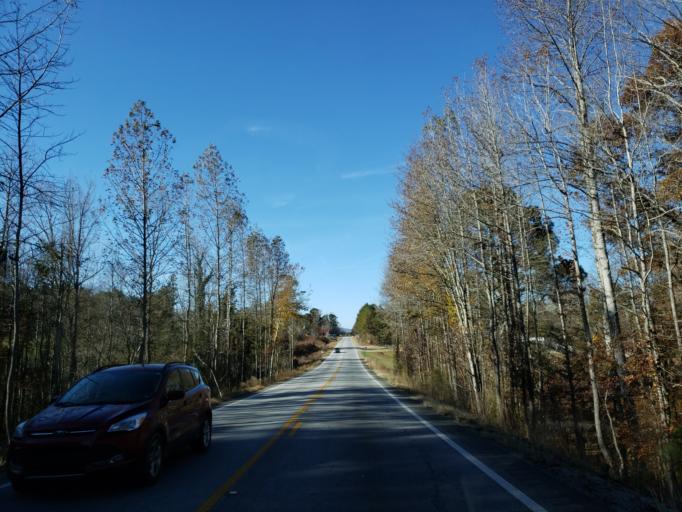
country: US
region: Alabama
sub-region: Calhoun County
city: Choccolocco
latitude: 33.5820
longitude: -85.6771
